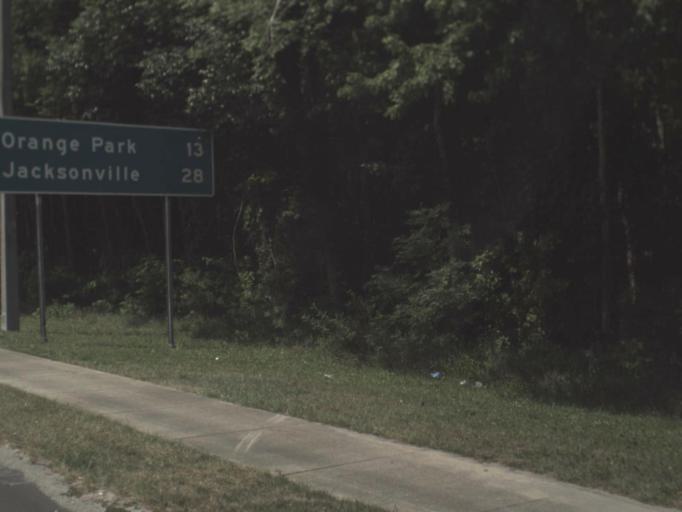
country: US
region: Florida
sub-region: Clay County
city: Green Cove Springs
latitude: 29.9844
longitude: -81.6763
